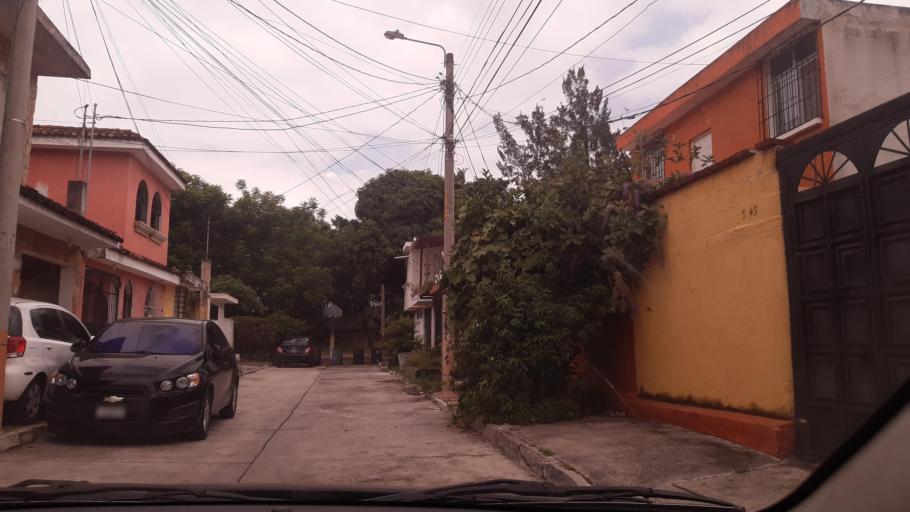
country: GT
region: Guatemala
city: Petapa
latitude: 14.5064
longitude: -90.5466
